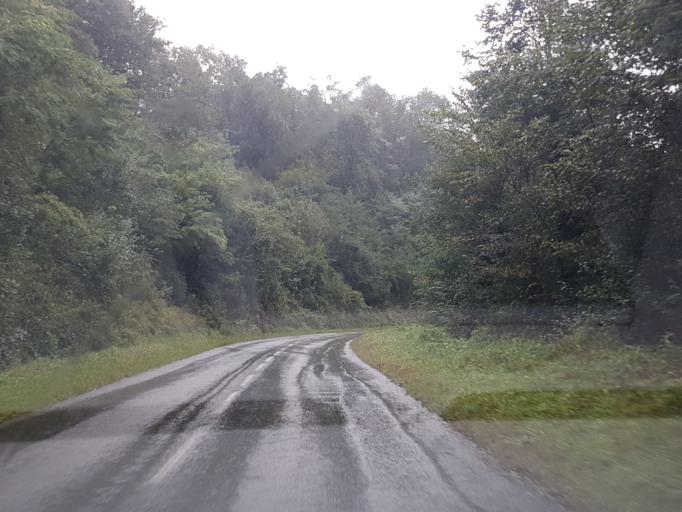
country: FR
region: Midi-Pyrenees
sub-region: Departement de l'Ariege
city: Montjoie-en-Couserans
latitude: 42.8962
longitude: 1.3603
